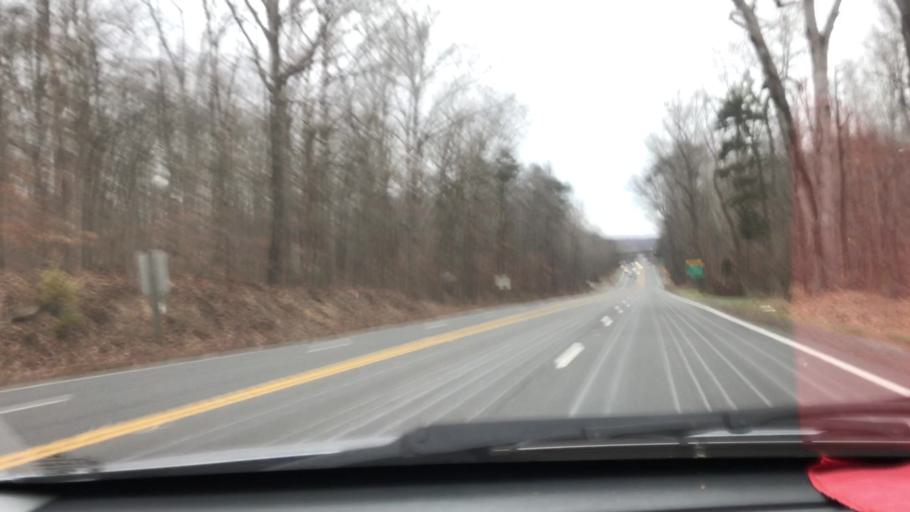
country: US
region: Virginia
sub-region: Prince William County
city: Triangle
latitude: 38.5266
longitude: -77.3551
